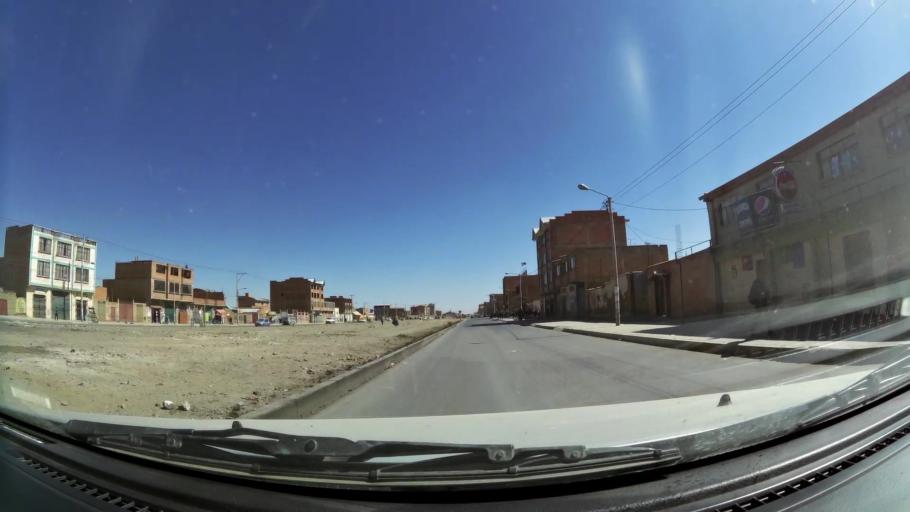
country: BO
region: La Paz
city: La Paz
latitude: -16.5391
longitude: -68.2022
